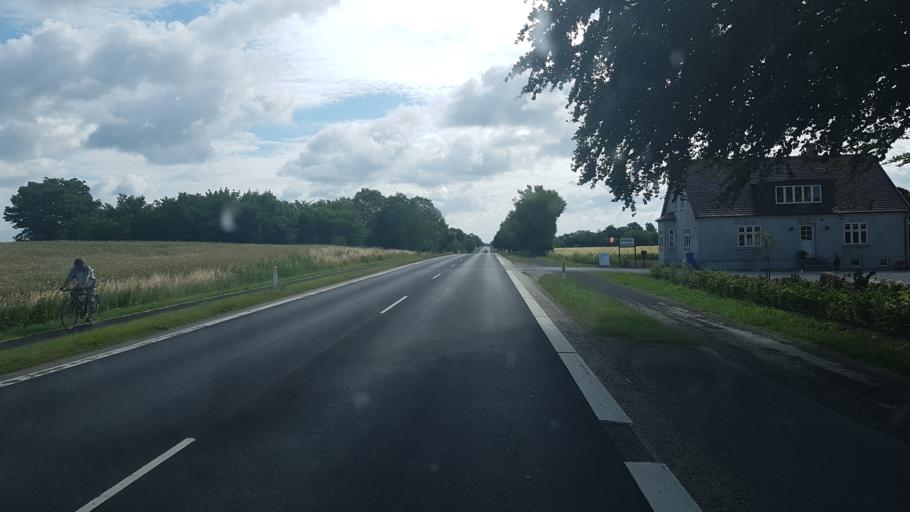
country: DK
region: South Denmark
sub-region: Kerteminde Kommune
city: Langeskov
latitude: 55.3617
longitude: 10.6099
